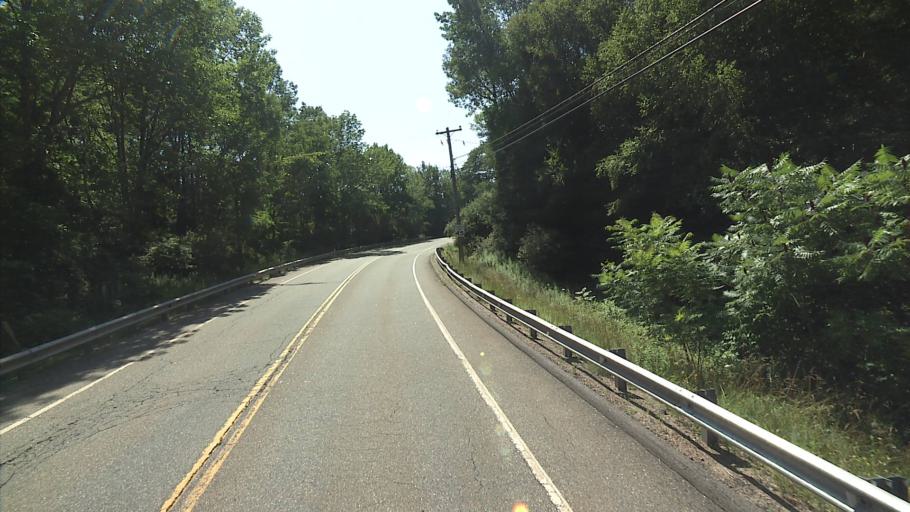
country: US
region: Connecticut
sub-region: Litchfield County
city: New Preston
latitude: 41.7885
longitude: -73.3615
